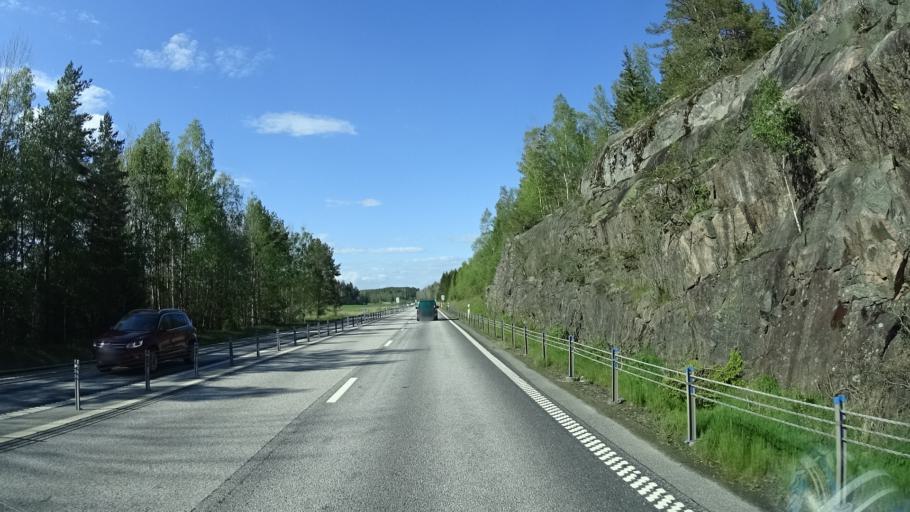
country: SE
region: OEstergoetland
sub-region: Valdemarsviks Kommun
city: Valdemarsvik
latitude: 58.2038
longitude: 16.5566
